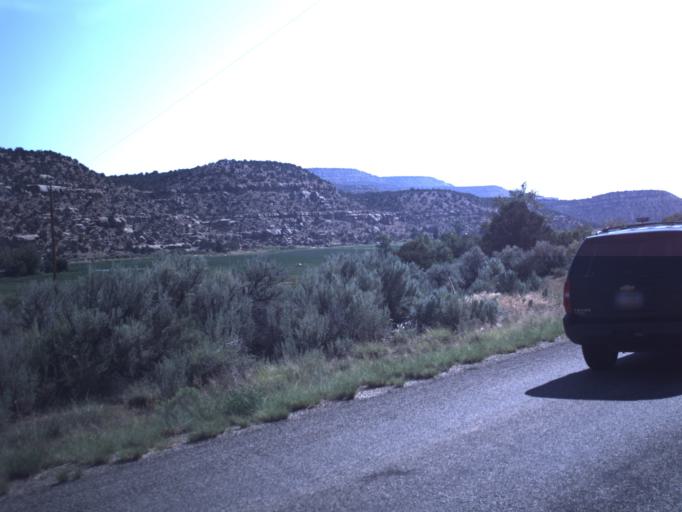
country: US
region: Utah
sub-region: Duchesne County
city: Duchesne
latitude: 40.2967
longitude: -110.5161
